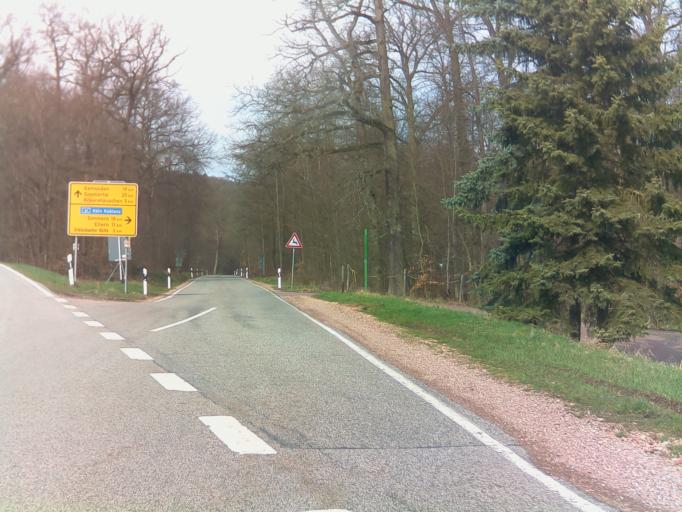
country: DE
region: Rheinland-Pfalz
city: Munchwald
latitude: 49.9018
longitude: 7.6790
